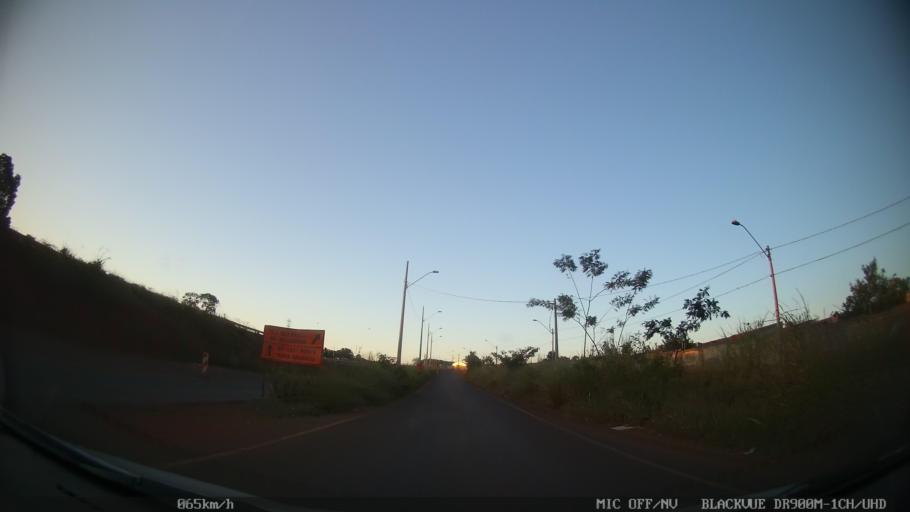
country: BR
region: Sao Paulo
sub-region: Sao Jose Do Rio Preto
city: Sao Jose do Rio Preto
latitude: -20.7743
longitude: -49.3515
